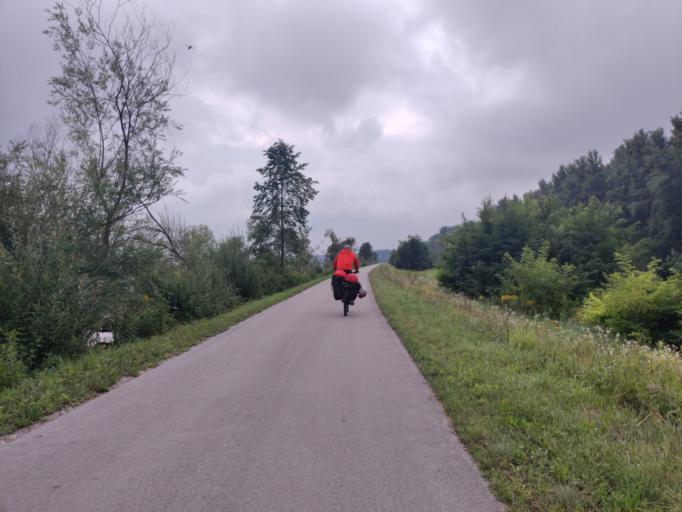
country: AT
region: Lower Austria
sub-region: Politischer Bezirk Sankt Polten
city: Traismauer
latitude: 48.3785
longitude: 15.7285
